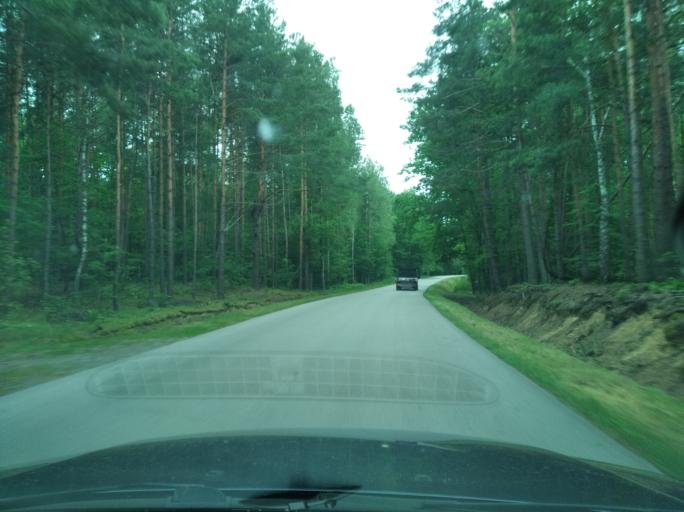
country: PL
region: Subcarpathian Voivodeship
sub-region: Powiat kolbuszowski
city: Niwiska
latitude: 50.2090
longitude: 21.6389
